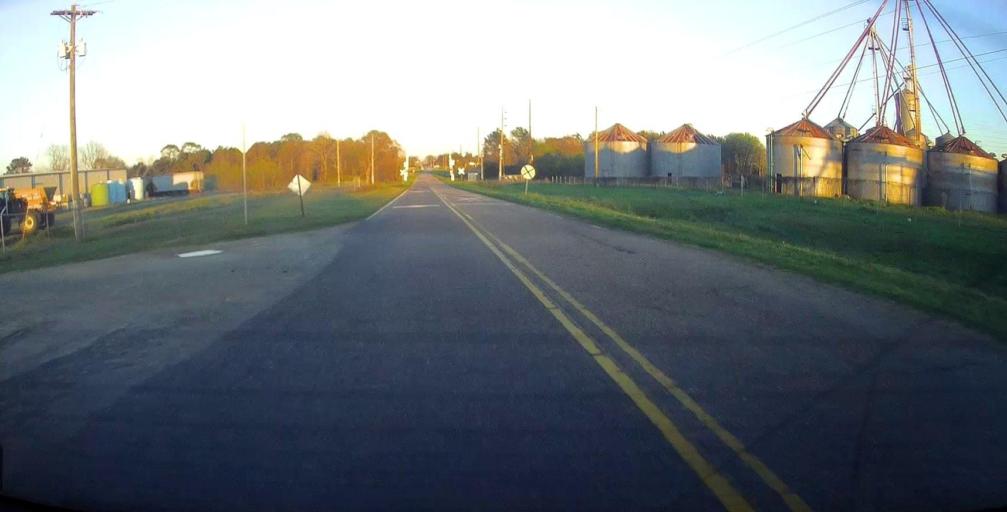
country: US
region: Georgia
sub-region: Crisp County
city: Cordele
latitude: 31.9554
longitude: -83.8063
